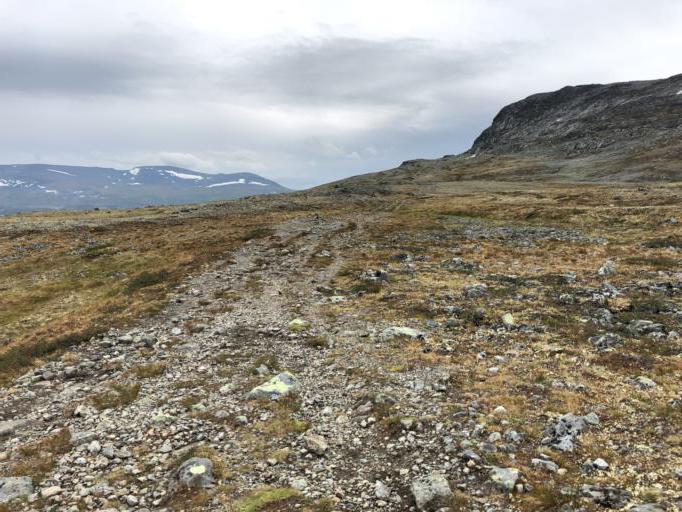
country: NO
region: Oppland
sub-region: Lom
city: Fossbergom
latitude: 61.5216
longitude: 8.8103
